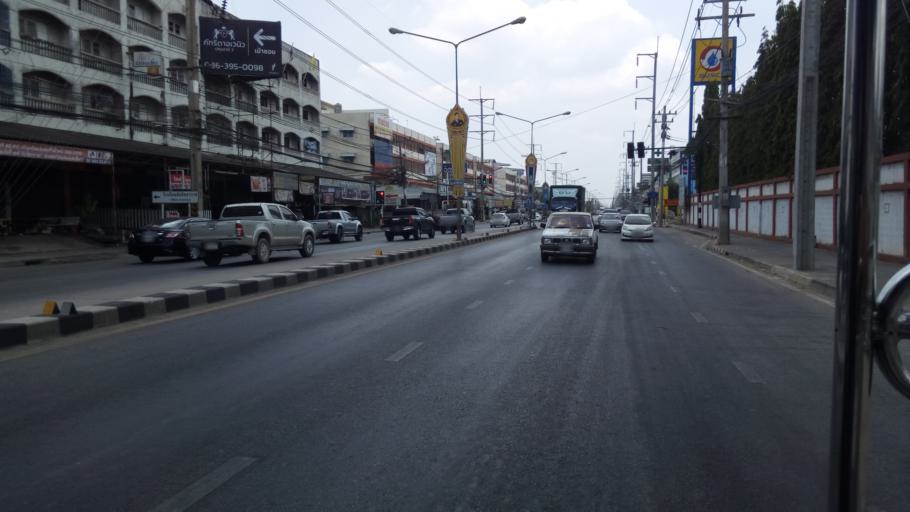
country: TH
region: Pathum Thani
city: Sam Khok
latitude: 14.0442
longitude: 100.5251
